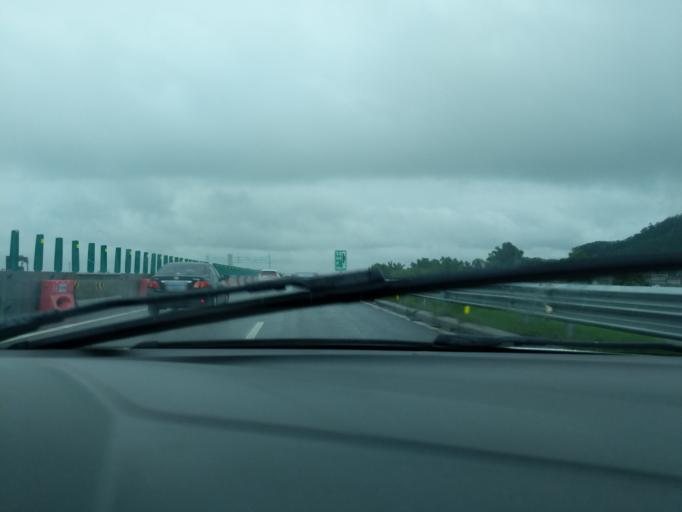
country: CN
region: Guangdong
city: Yueshan
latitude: 22.4652
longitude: 112.7018
